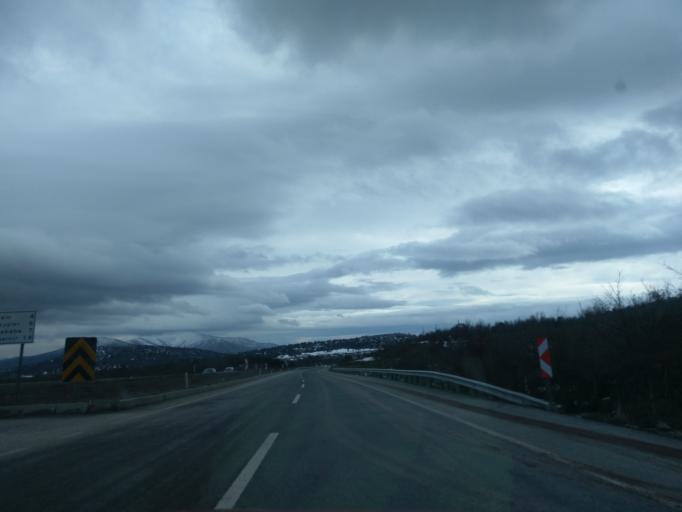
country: TR
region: Kuetahya
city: Aslanapa
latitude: 39.2749
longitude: 29.9179
